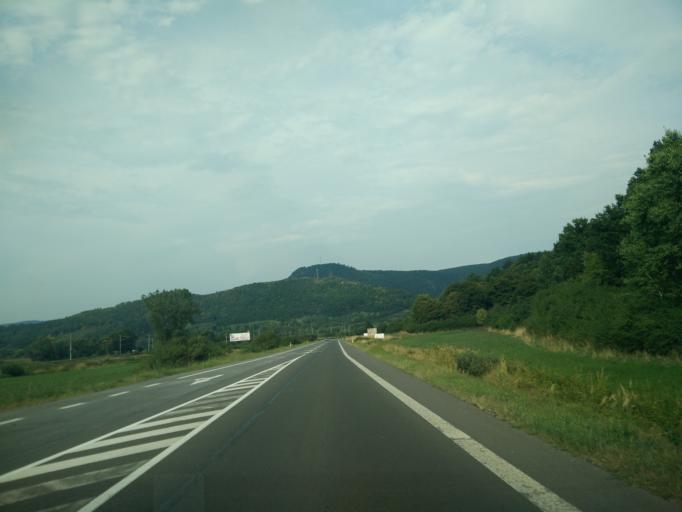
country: SK
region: Banskobystricky
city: Ziar nad Hronom
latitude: 48.5840
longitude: 18.8791
